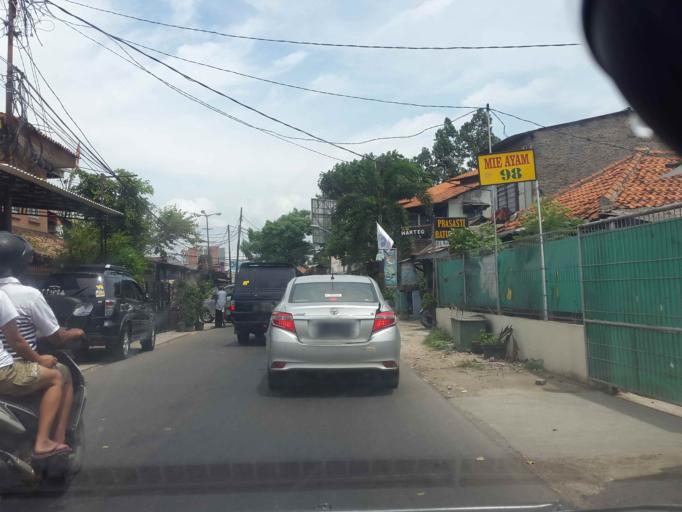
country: ID
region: Banten
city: Tangerang
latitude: -6.1673
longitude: 106.6348
